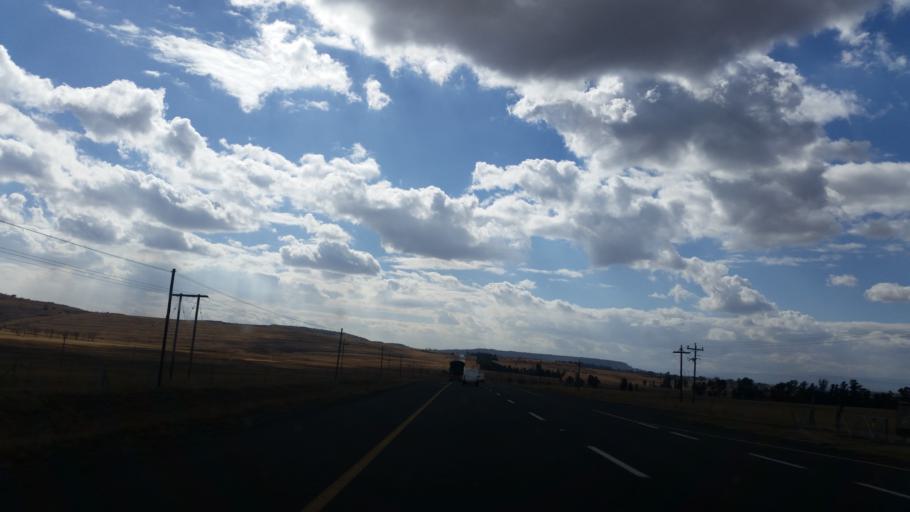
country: ZA
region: KwaZulu-Natal
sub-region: Amajuba District Municipality
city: Newcastle
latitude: -27.8719
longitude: 29.9635
